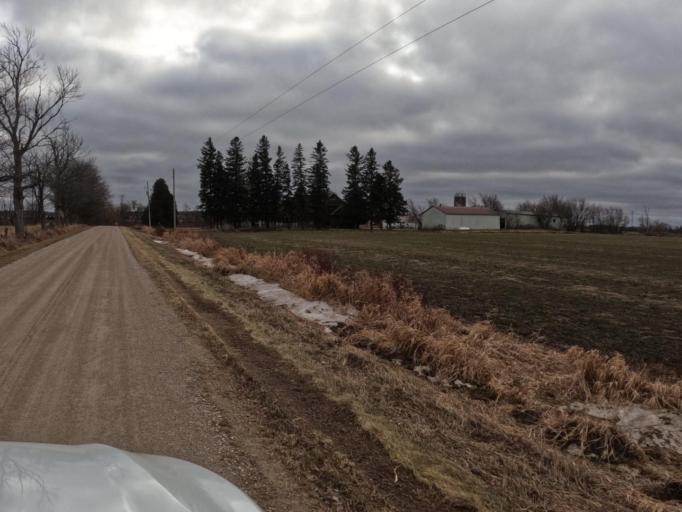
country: CA
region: Ontario
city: Shelburne
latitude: 43.8894
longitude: -80.3287
